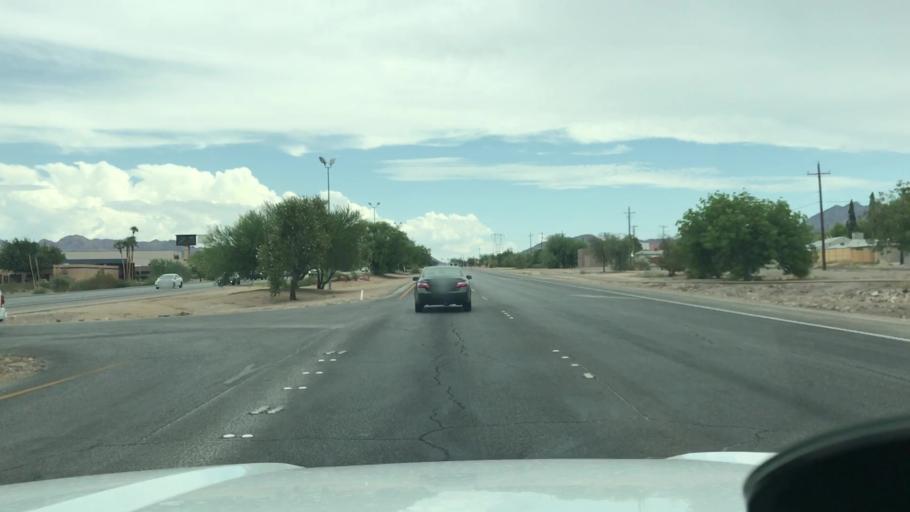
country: US
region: Nevada
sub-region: Clark County
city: Henderson
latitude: 36.0287
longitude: -114.9700
